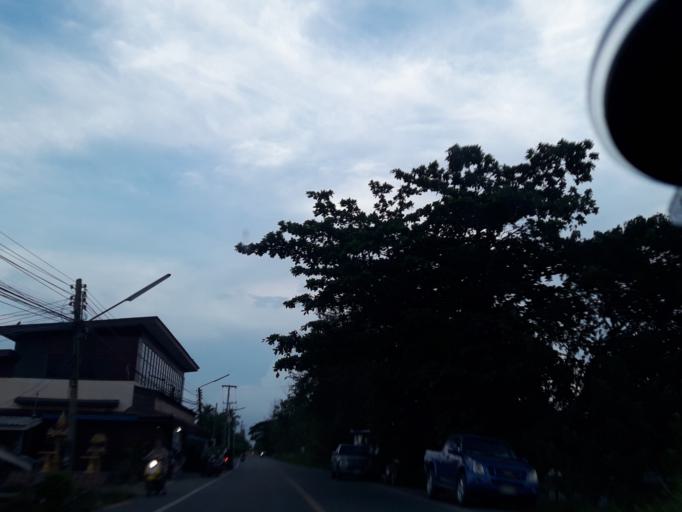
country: TH
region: Pathum Thani
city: Nong Suea
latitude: 14.1304
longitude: 100.8690
